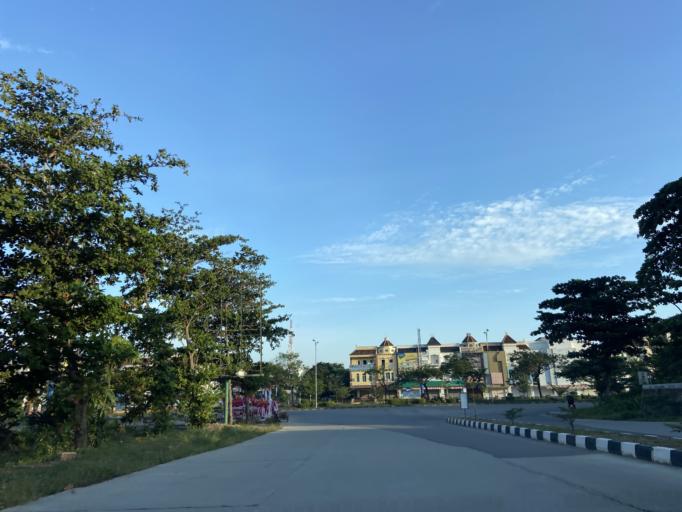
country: SG
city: Singapore
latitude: 1.1287
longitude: 104.0386
